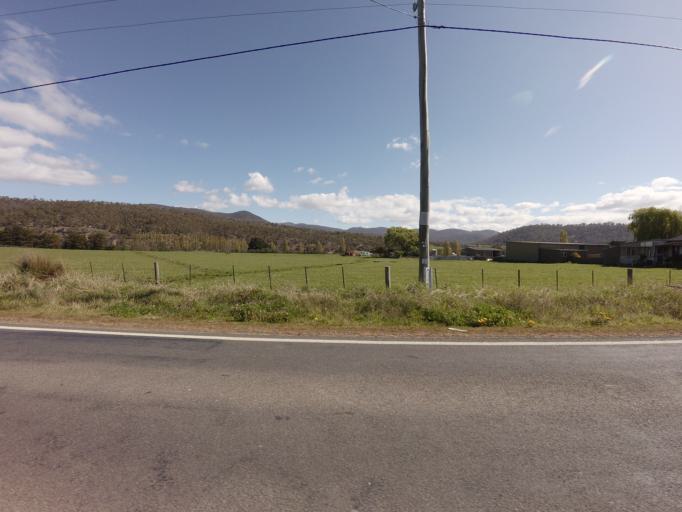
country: AU
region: Tasmania
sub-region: Derwent Valley
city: New Norfolk
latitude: -42.7737
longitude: 147.0348
